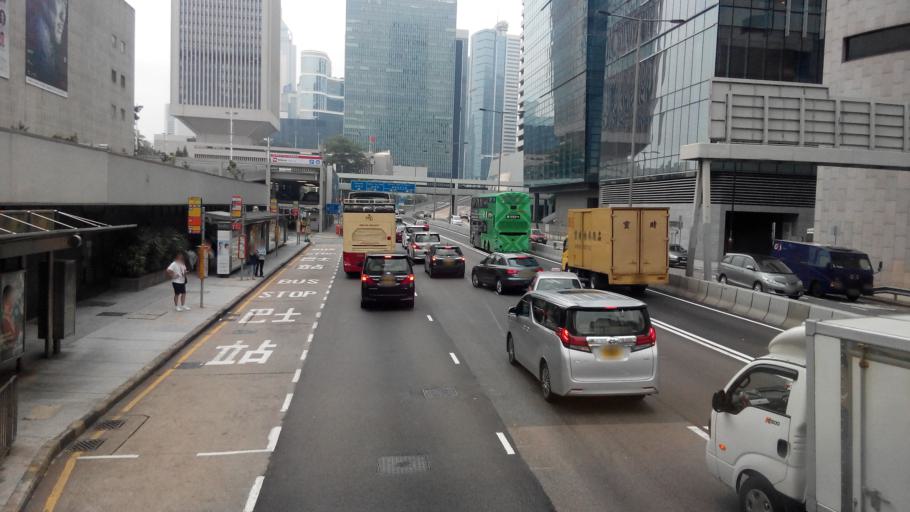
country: HK
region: Central and Western
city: Central
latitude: 22.2819
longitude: 114.1609
